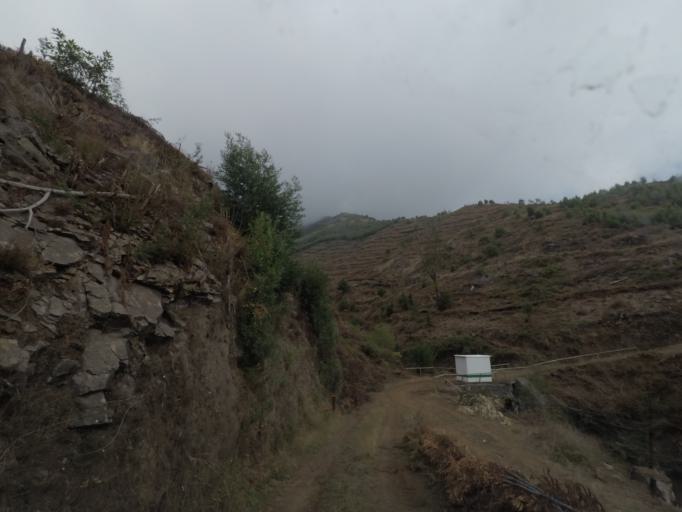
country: PT
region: Madeira
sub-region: Funchal
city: Nossa Senhora do Monte
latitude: 32.6955
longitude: -16.9111
